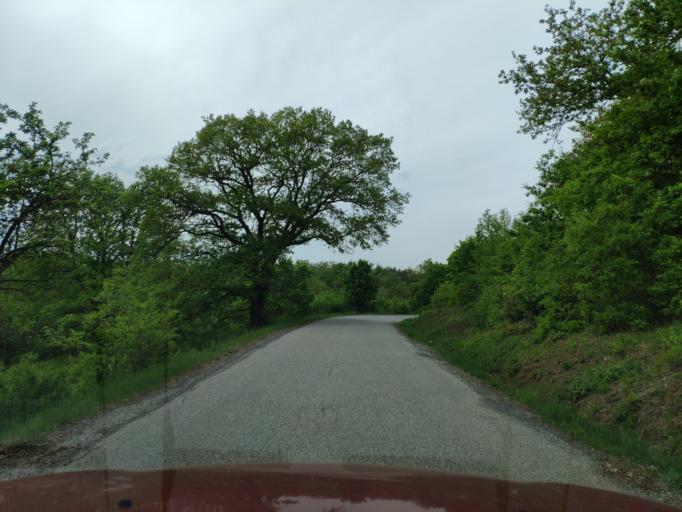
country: SK
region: Banskobystricky
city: Rimavska Sobota
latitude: 48.4985
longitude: 20.0959
